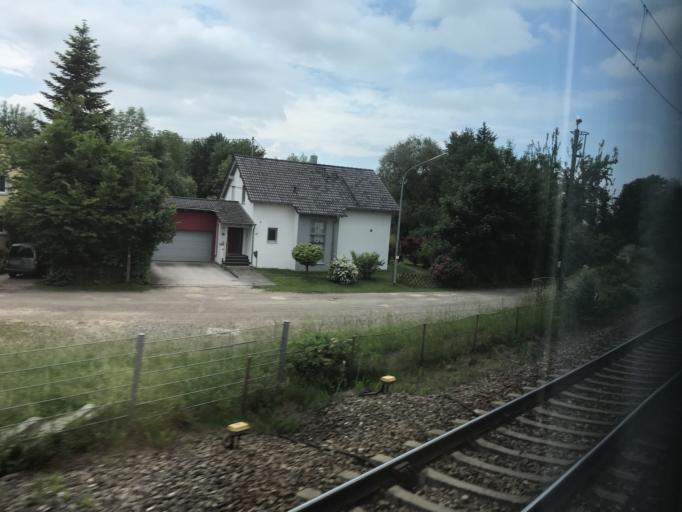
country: DE
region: Bavaria
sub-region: Swabia
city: Nersingen
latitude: 48.4318
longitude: 10.1228
